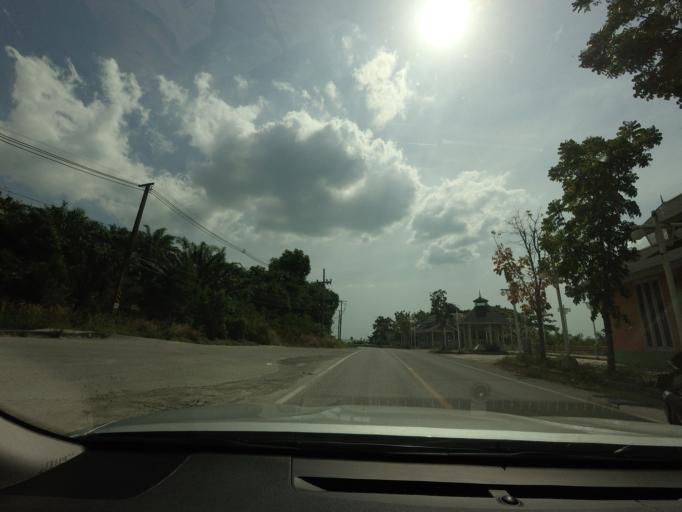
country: TH
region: Phangnga
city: Ban Ao Nang
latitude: 8.0667
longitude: 98.7441
